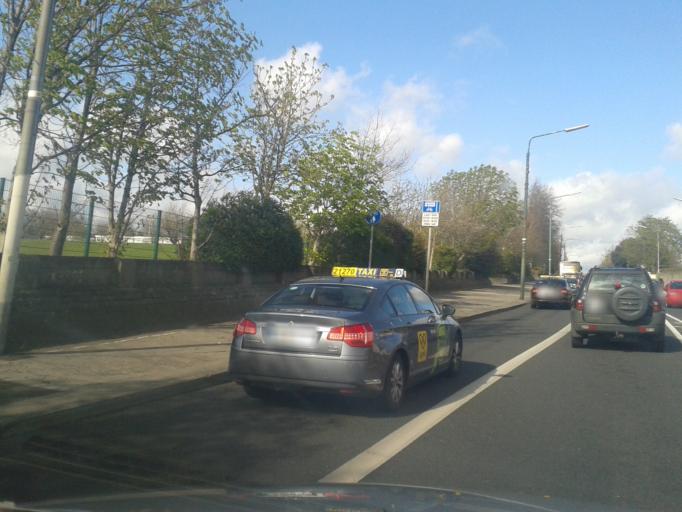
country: IE
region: Leinster
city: Drumcondra
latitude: 53.3778
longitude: -6.2481
